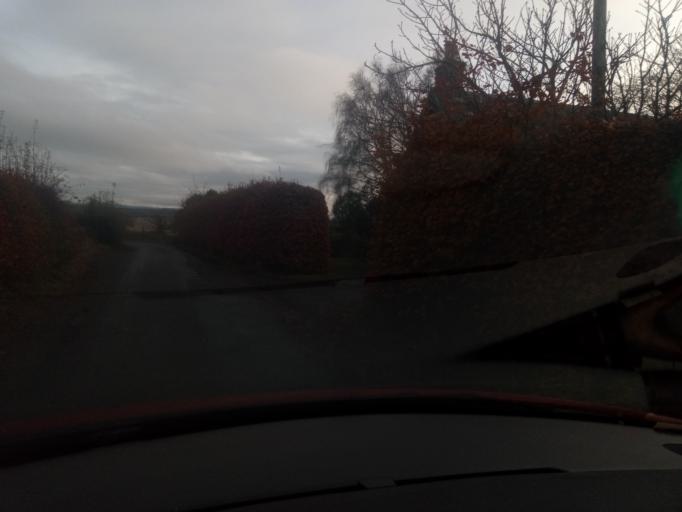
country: GB
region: Scotland
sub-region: The Scottish Borders
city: Jedburgh
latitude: 55.4785
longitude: -2.5683
